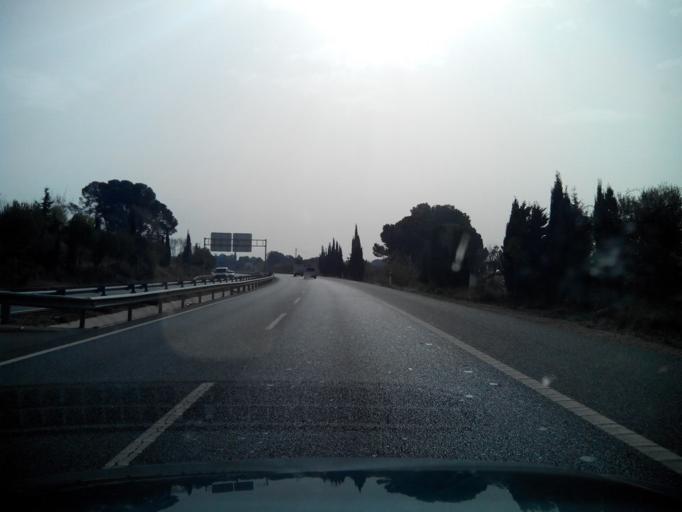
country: ES
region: Catalonia
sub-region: Provincia de Tarragona
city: Reus
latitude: 41.1337
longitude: 1.1037
